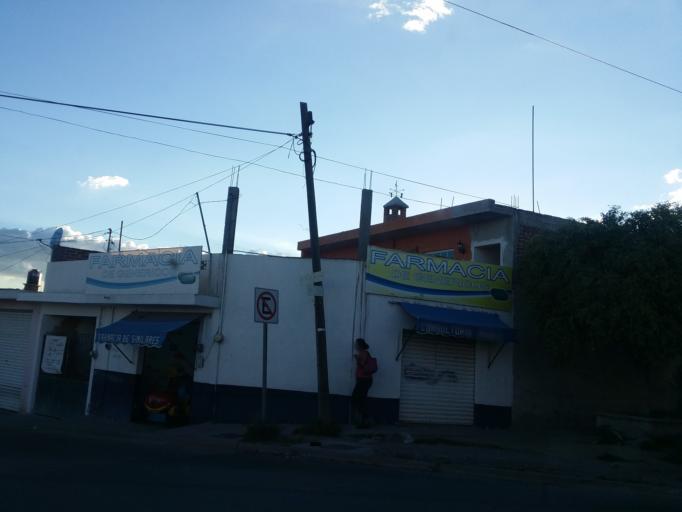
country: MX
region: Guanajuato
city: Leon
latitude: 21.2042
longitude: -101.6773
